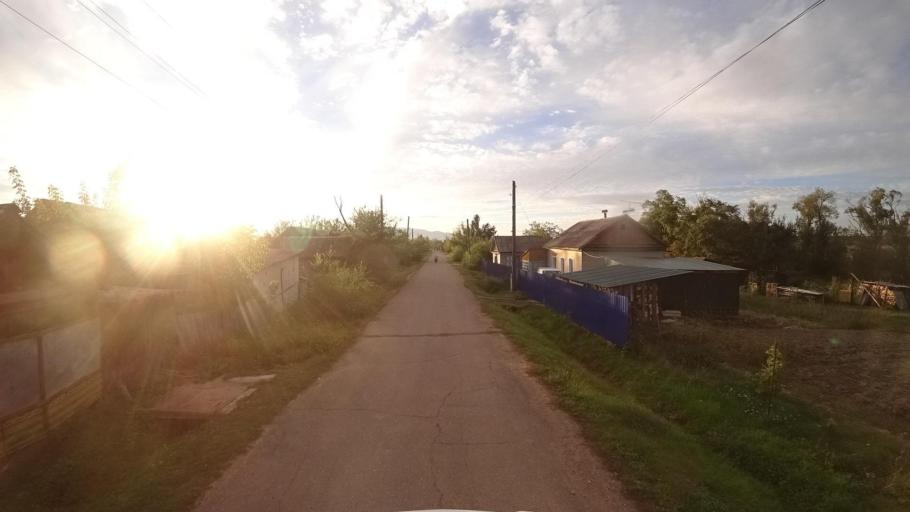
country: RU
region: Primorskiy
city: Yakovlevka
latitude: 44.4230
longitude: 133.4890
